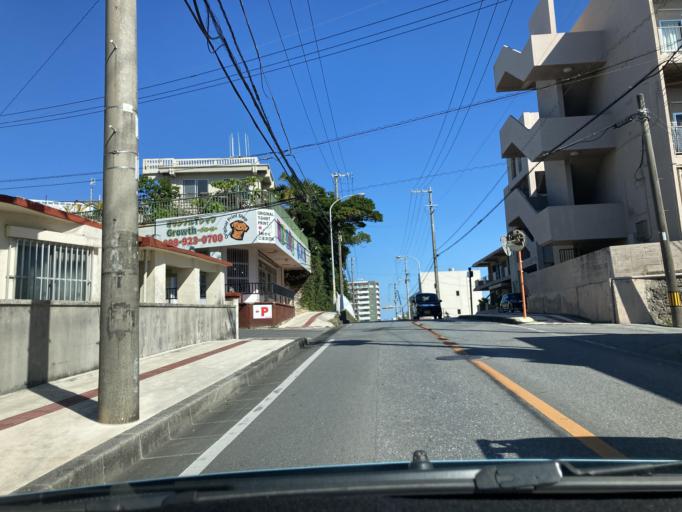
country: JP
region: Okinawa
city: Okinawa
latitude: 26.3298
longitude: 127.8042
